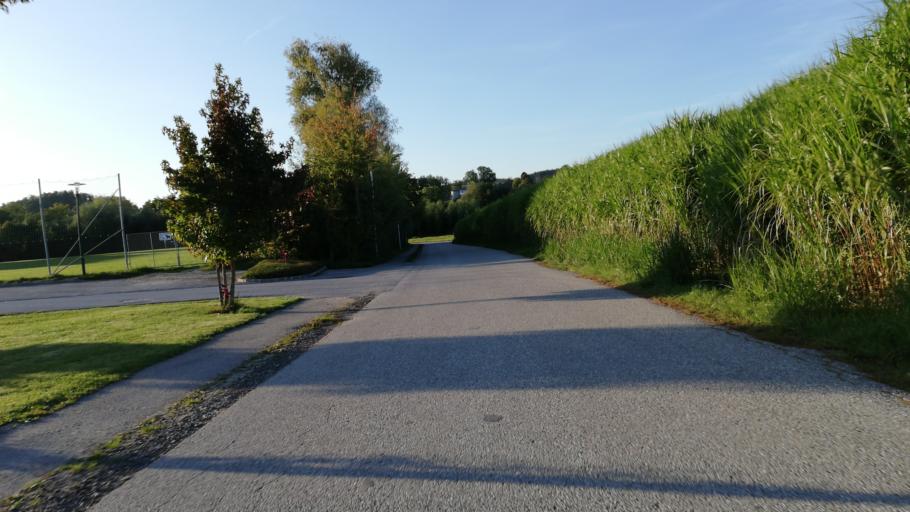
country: AT
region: Upper Austria
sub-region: Politischer Bezirk Grieskirchen
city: Bad Schallerbach
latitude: 48.1858
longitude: 13.9036
